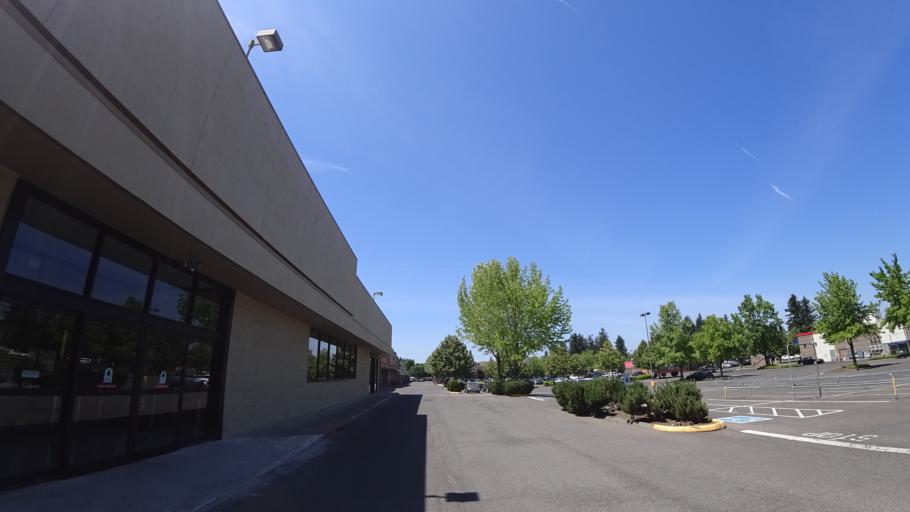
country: US
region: Oregon
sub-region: Multnomah County
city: Gresham
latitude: 45.4914
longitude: -122.4862
